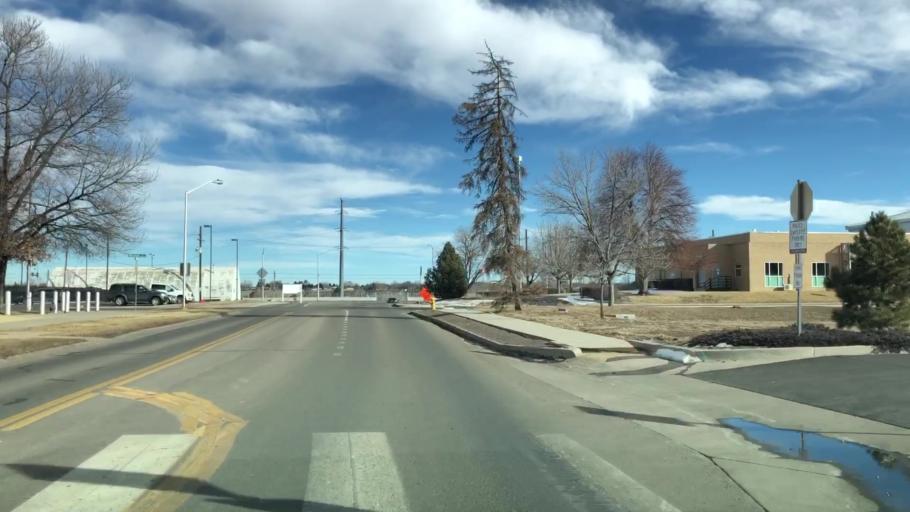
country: US
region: Colorado
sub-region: Adams County
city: Aurora
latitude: 39.7477
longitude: -104.8316
